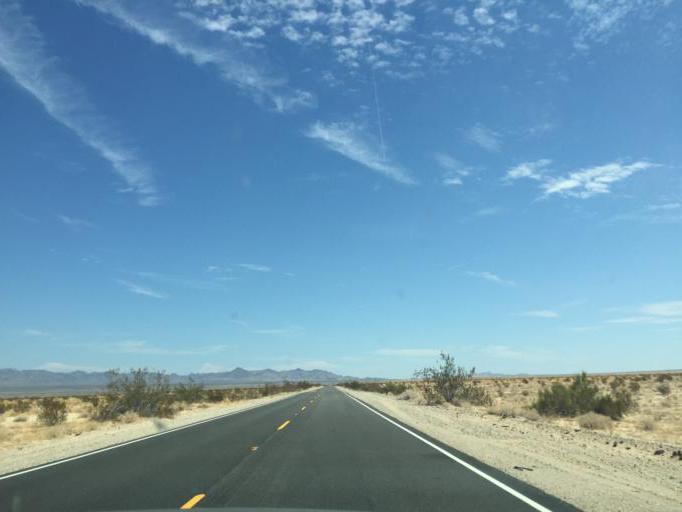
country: US
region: California
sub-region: Riverside County
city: Mesa Verde
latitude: 34.0968
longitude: -115.0302
